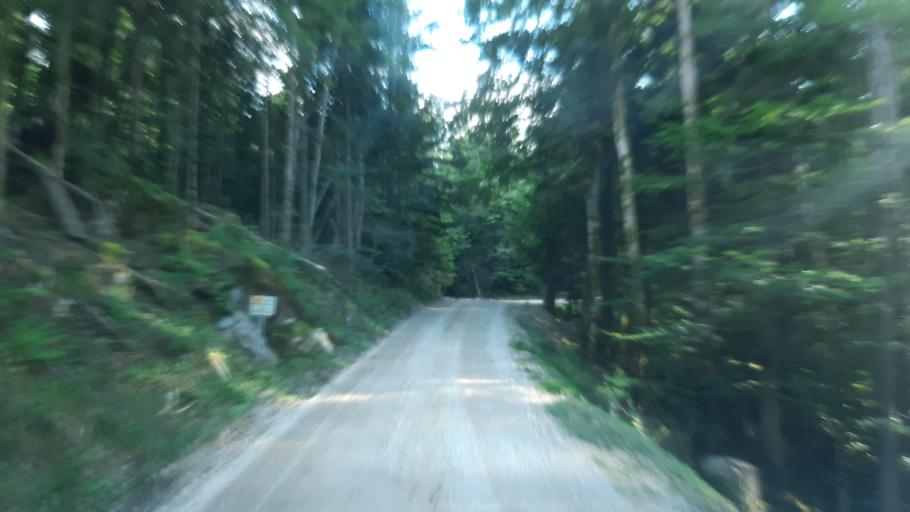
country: SI
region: Dolenjske Toplice
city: Dolenjske Toplice
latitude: 45.6999
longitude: 15.0117
